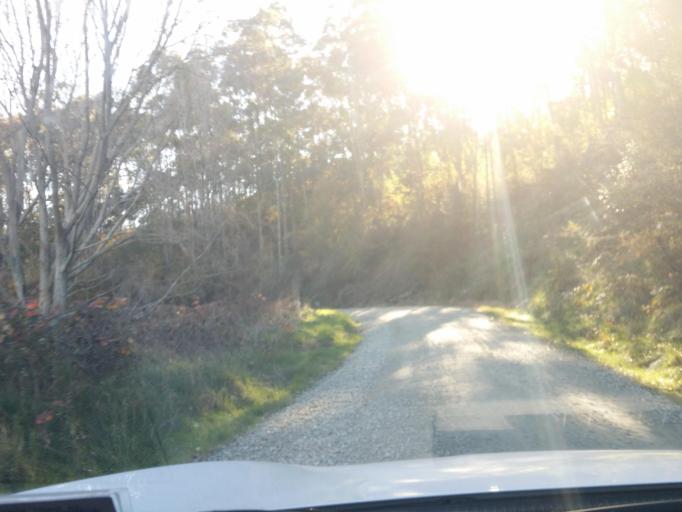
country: NZ
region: Gisborne
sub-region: Gisborne District
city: Gisborne
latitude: -38.6089
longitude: 177.8767
